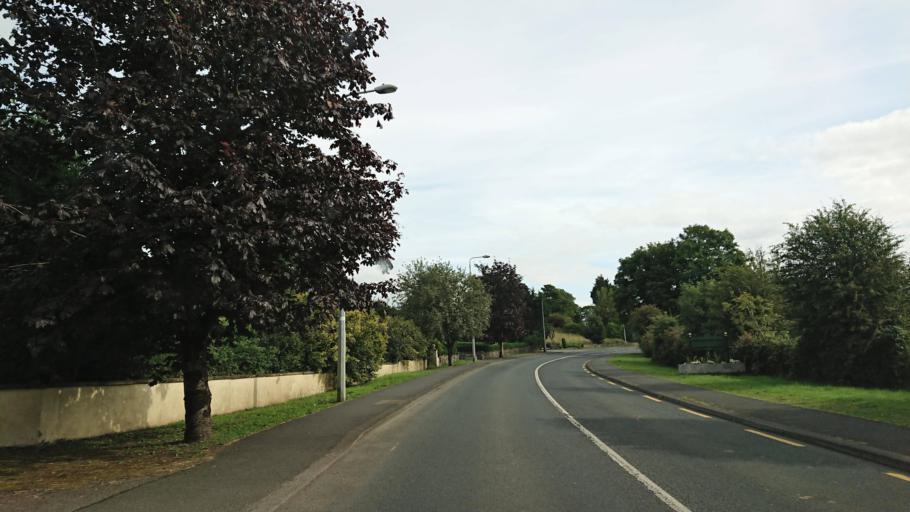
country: IE
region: Connaught
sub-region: County Leitrim
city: Carrick-on-Shannon
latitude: 53.9881
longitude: -8.0636
